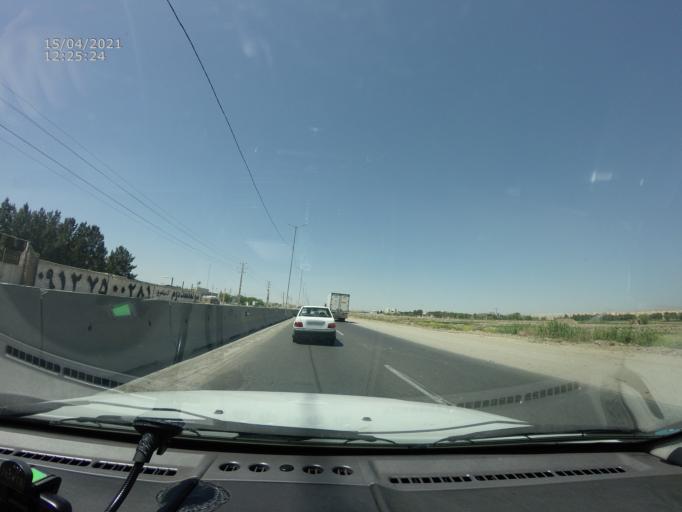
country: IR
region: Tehran
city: Eslamshahr
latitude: 35.5123
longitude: 51.2463
